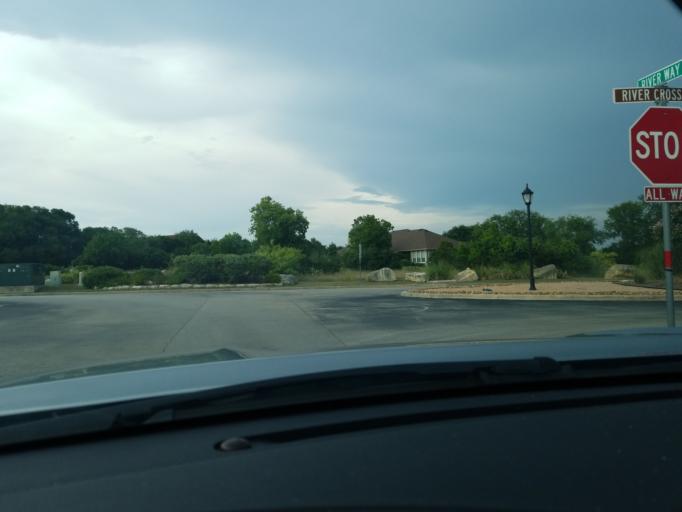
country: US
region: Texas
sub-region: Comal County
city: Bulverde
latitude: 29.8472
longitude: -98.4030
